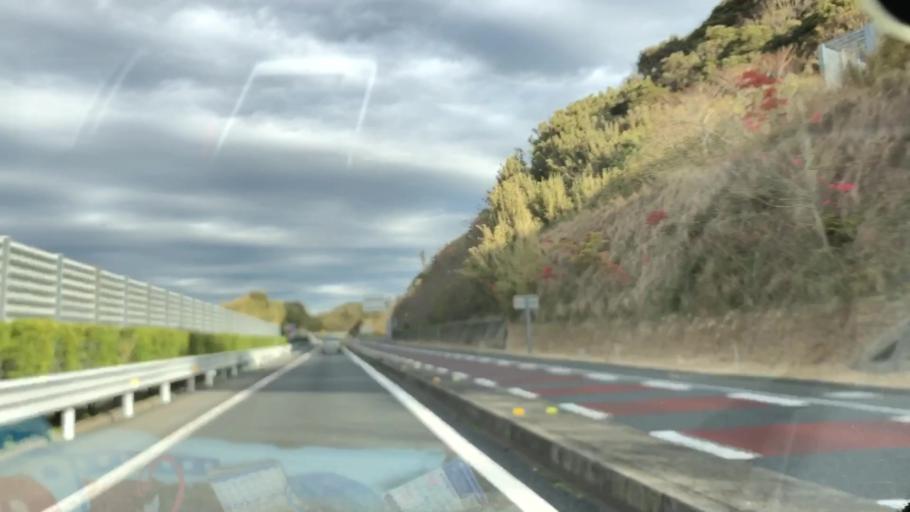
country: JP
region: Chiba
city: Tateyama
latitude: 35.0446
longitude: 139.8533
